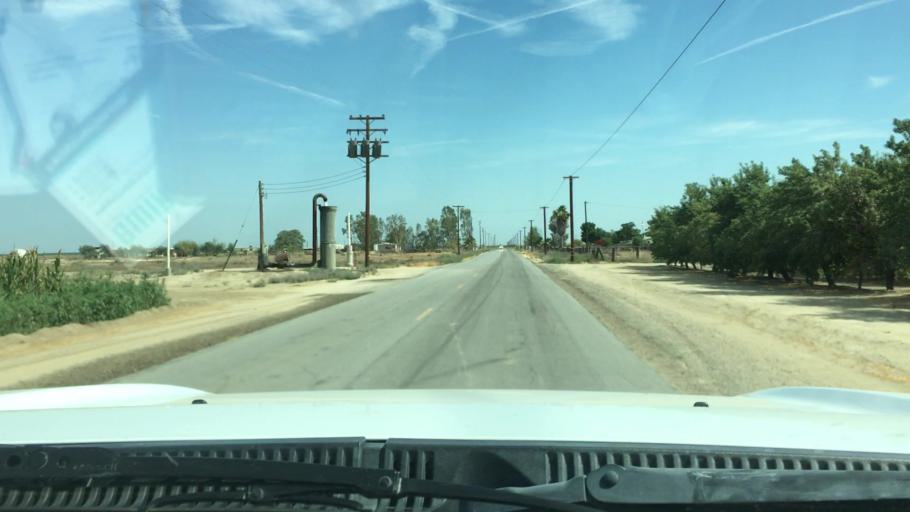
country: US
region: California
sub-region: Kern County
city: Buttonwillow
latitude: 35.4270
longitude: -119.3762
